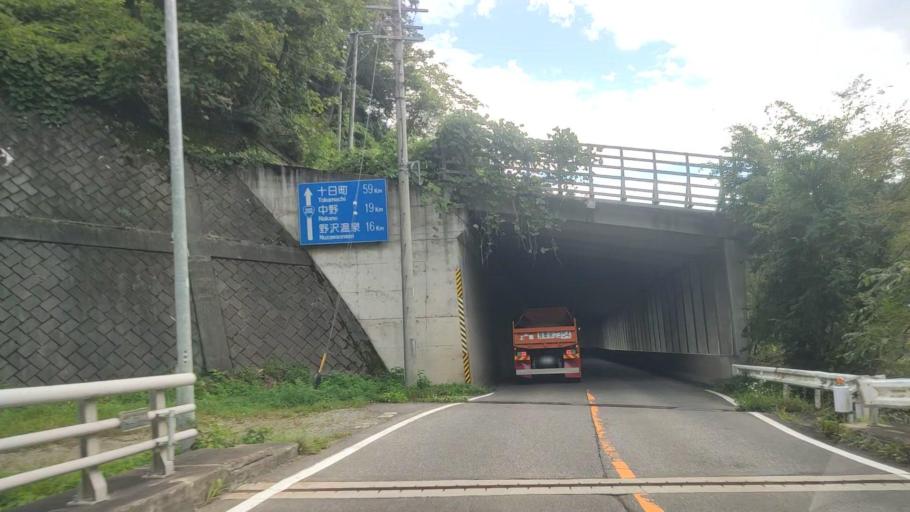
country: JP
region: Nagano
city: Iiyama
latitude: 36.8693
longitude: 138.3244
